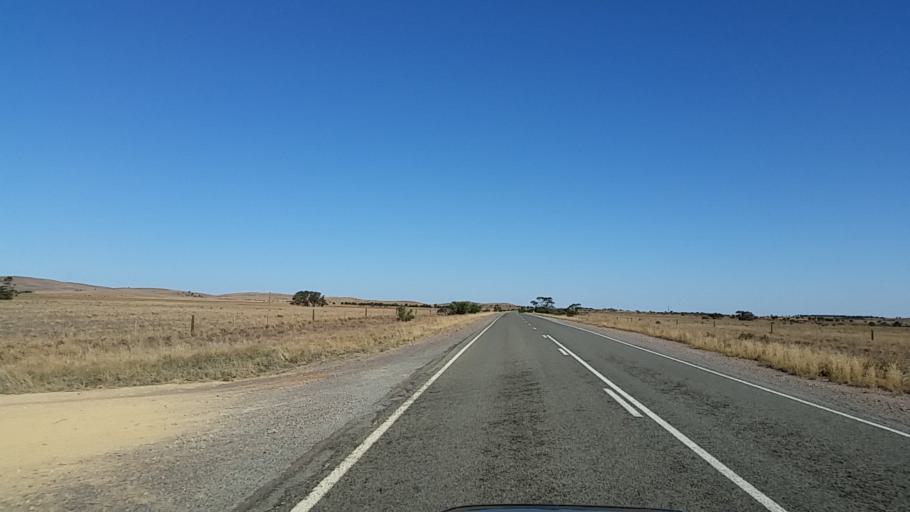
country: AU
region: South Australia
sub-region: Peterborough
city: Peterborough
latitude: -32.5355
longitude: 138.5565
